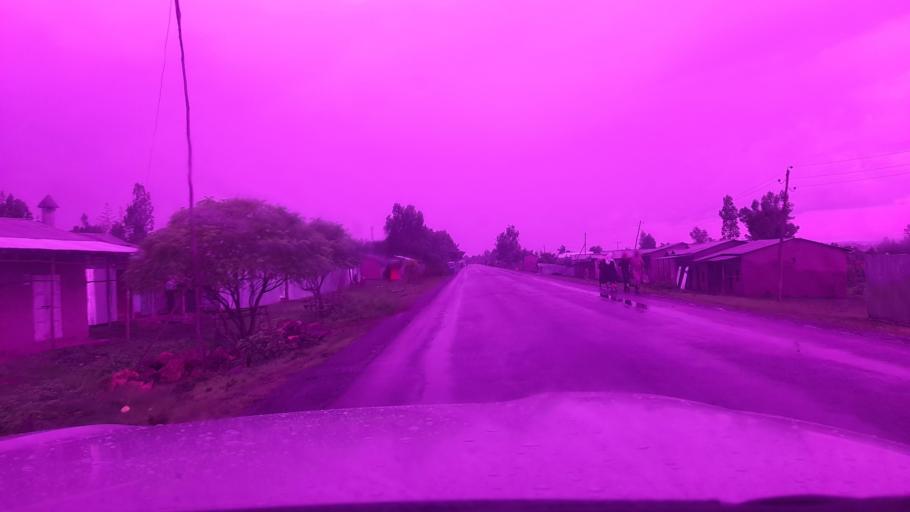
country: ET
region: Oromiya
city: Jima
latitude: 7.7153
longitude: 37.0998
